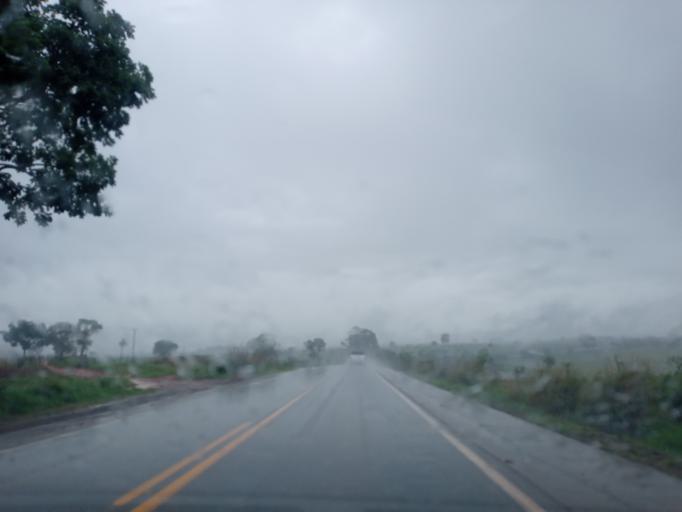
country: BR
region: Minas Gerais
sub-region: Luz
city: Luz
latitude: -19.7727
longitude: -45.7768
